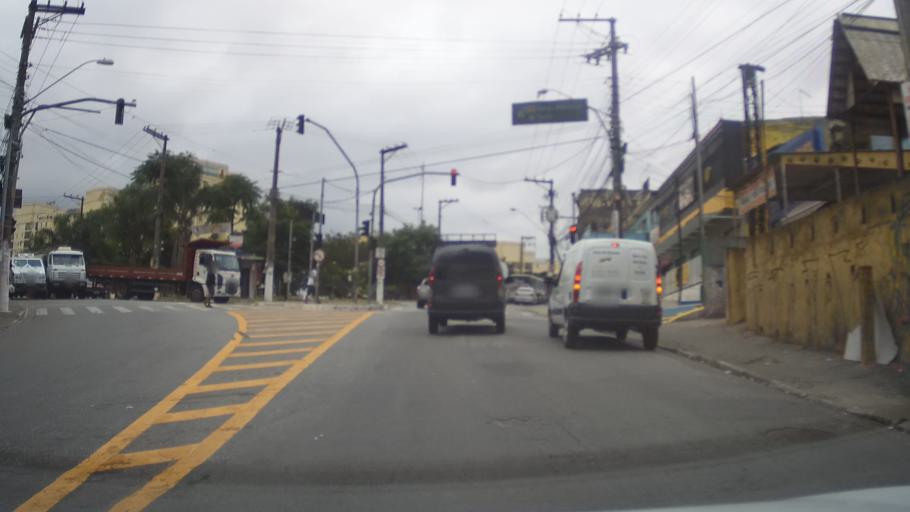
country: BR
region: Sao Paulo
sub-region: Itaquaquecetuba
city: Itaquaquecetuba
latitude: -23.4540
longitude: -46.4067
